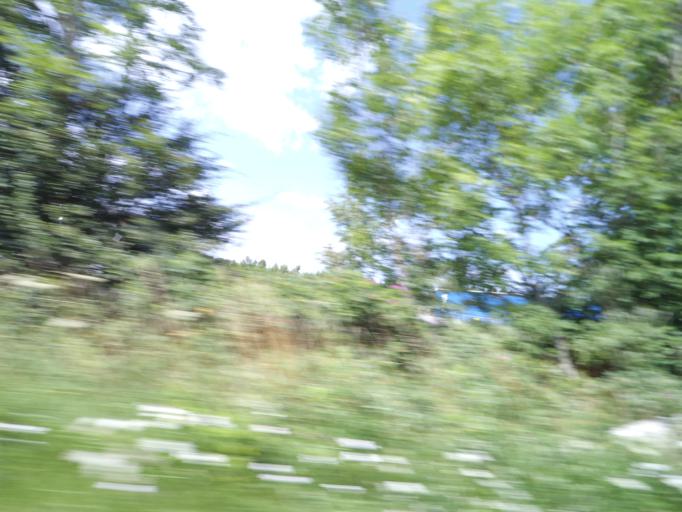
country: DK
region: South Denmark
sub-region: Assens Kommune
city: Arup
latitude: 55.3822
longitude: 10.0643
